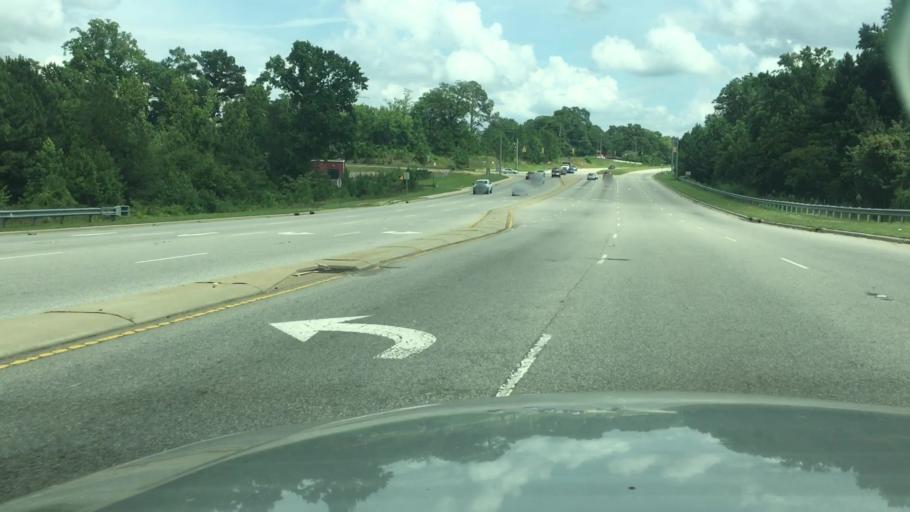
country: US
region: North Carolina
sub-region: Cumberland County
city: Hope Mills
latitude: 35.0026
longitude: -78.9782
